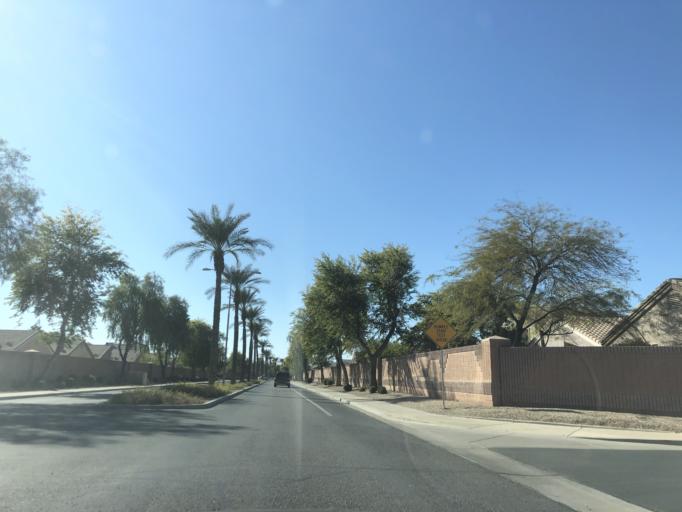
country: US
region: Arizona
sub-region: Maricopa County
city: El Mirage
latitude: 33.6186
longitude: -112.3290
